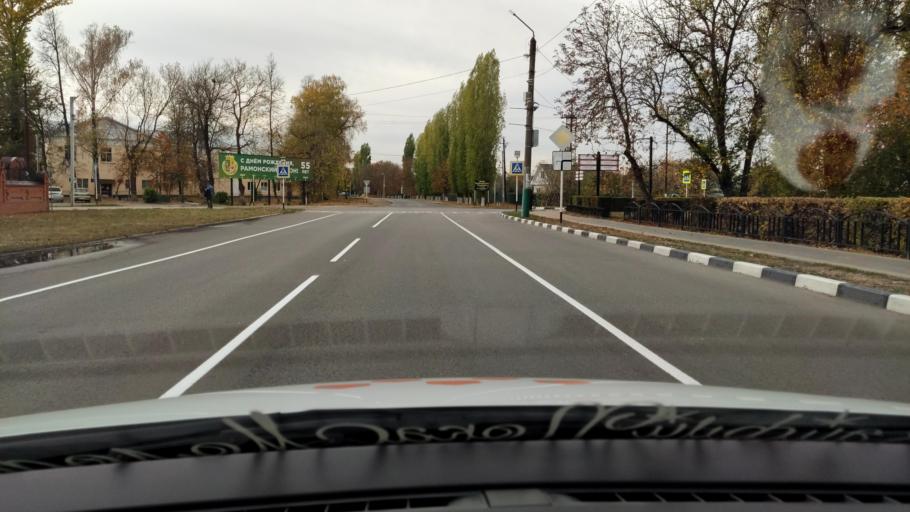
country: RU
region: Voronezj
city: Ramon'
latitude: 51.9094
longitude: 39.3366
